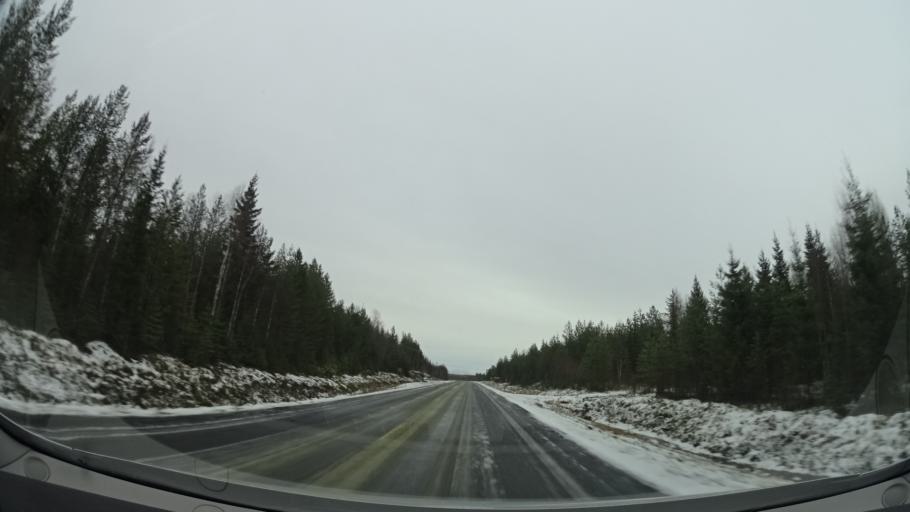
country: SE
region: Vaesterbotten
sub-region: Lycksele Kommun
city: Lycksele
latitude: 64.5309
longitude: 18.4628
